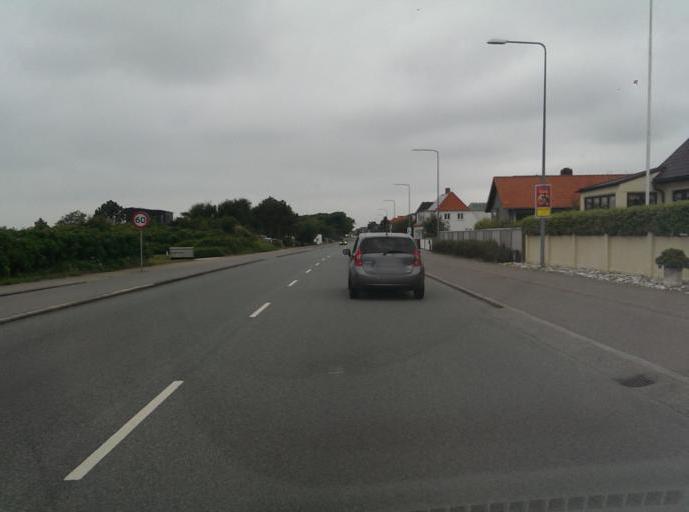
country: DK
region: South Denmark
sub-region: Fano Kommune
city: Nordby
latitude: 55.4901
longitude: 8.4080
